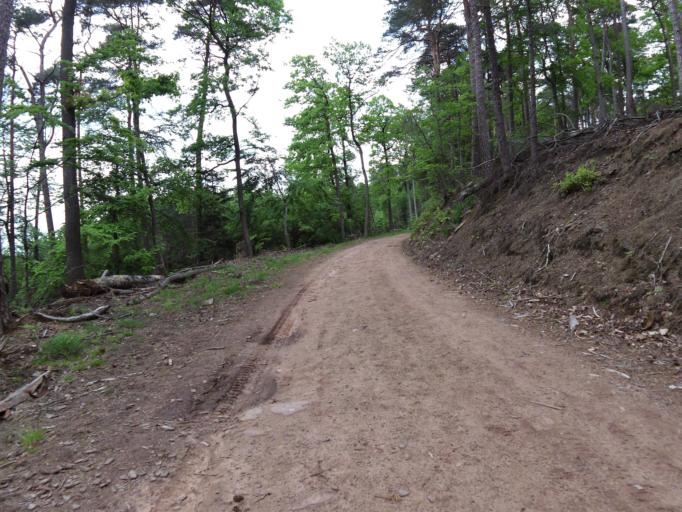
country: DE
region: Rheinland-Pfalz
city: Neidenfels
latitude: 49.4093
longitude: 8.0650
